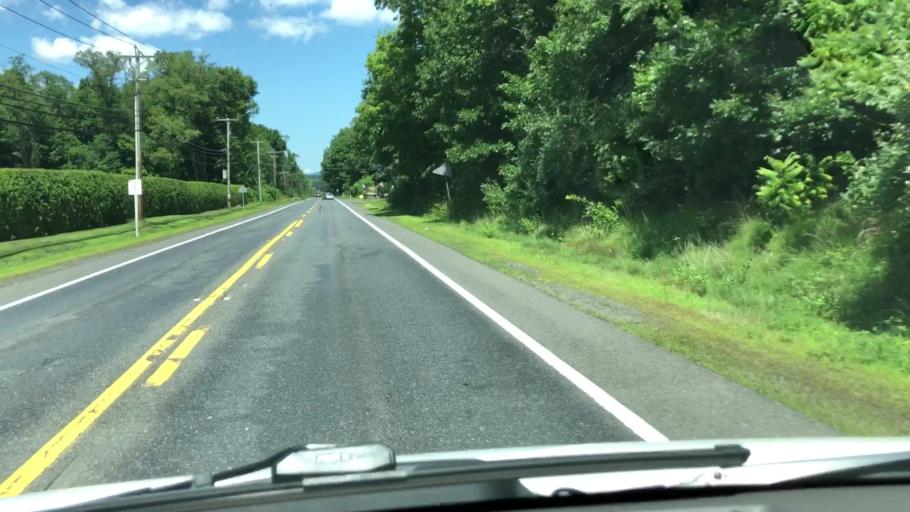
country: US
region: Massachusetts
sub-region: Franklin County
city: Greenfield
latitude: 42.5449
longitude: -72.6014
